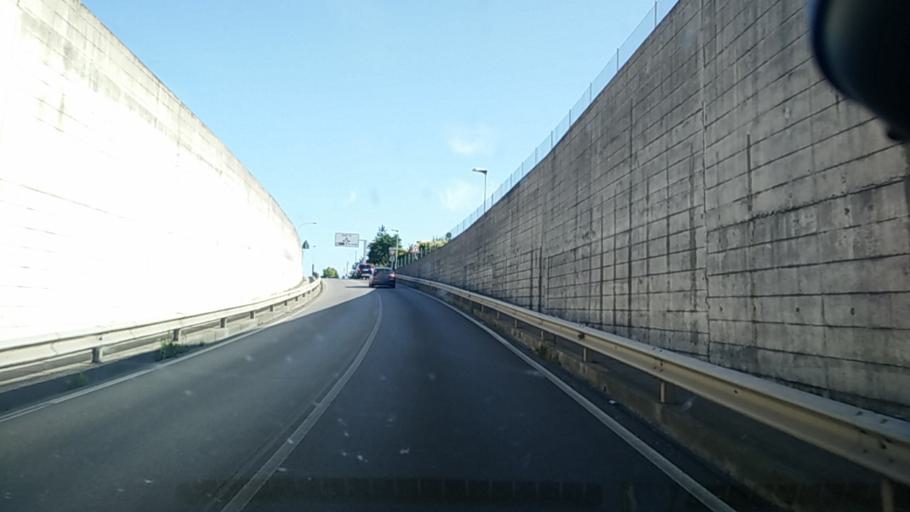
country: IT
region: Veneto
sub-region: Provincia di Treviso
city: San Floriano-Olmi
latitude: 45.6778
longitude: 12.3303
